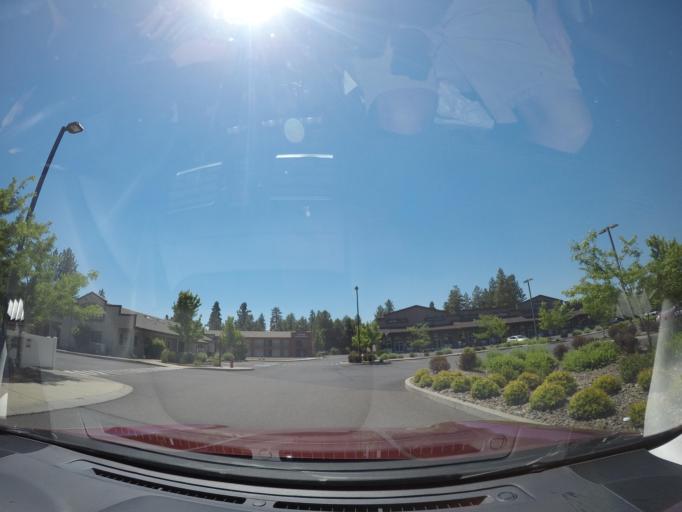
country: US
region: Oregon
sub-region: Deschutes County
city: Sisters
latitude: 44.2959
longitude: -121.5609
